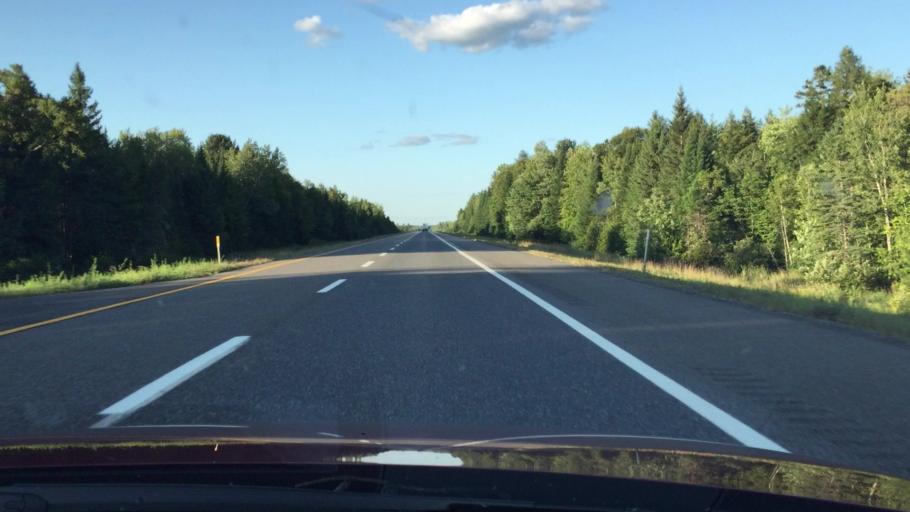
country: US
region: Maine
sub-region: Penobscot County
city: Patten
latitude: 46.0562
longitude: -68.2372
